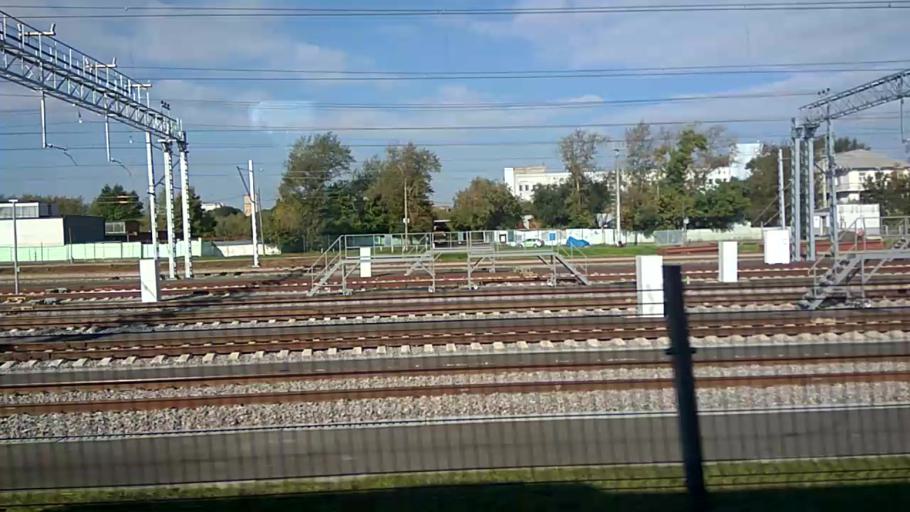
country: RU
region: Moscow
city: Ryazanskiy
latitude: 55.7395
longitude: 37.7334
